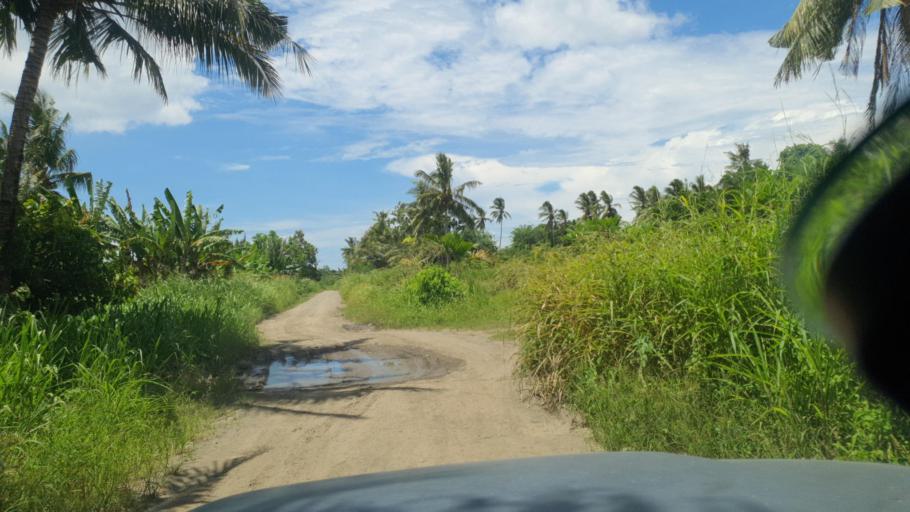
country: SB
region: Guadalcanal
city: Honiara
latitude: -9.4483
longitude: 160.1847
